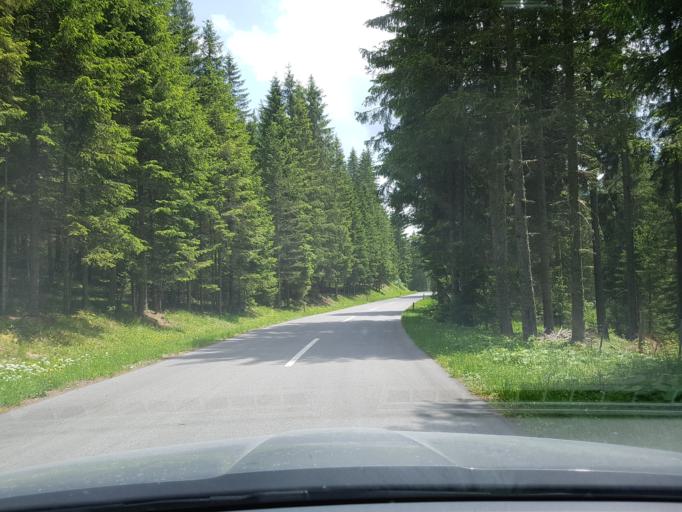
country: AT
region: Carinthia
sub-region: Politischer Bezirk Spittal an der Drau
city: Kleinkirchheim
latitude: 46.8878
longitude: 13.8434
